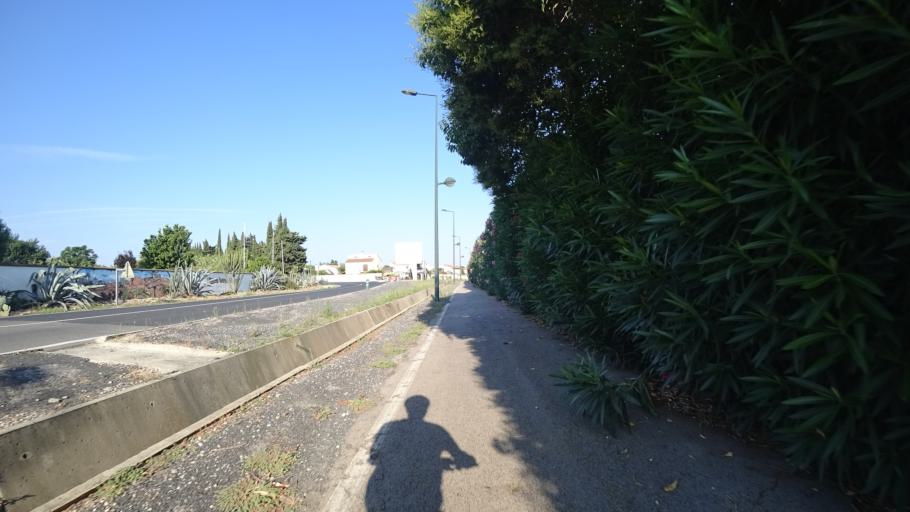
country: FR
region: Languedoc-Roussillon
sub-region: Departement des Pyrenees-Orientales
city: Bompas
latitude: 42.7214
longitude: 2.9314
